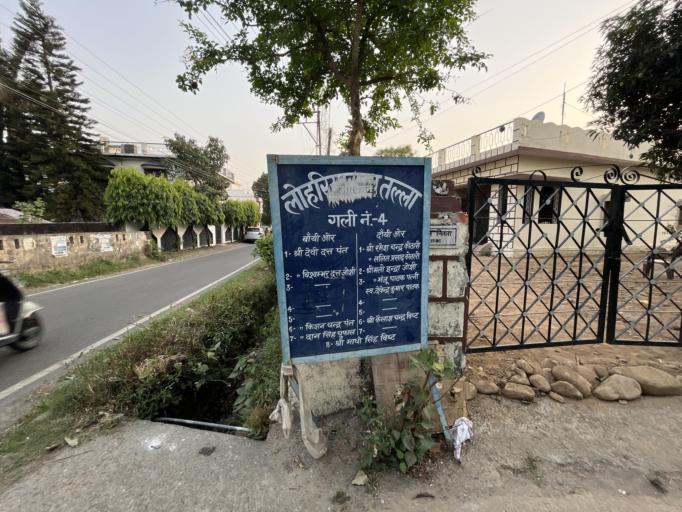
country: IN
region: Uttarakhand
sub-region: Naini Tal
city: Haldwani
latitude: 29.2244
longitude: 79.4949
